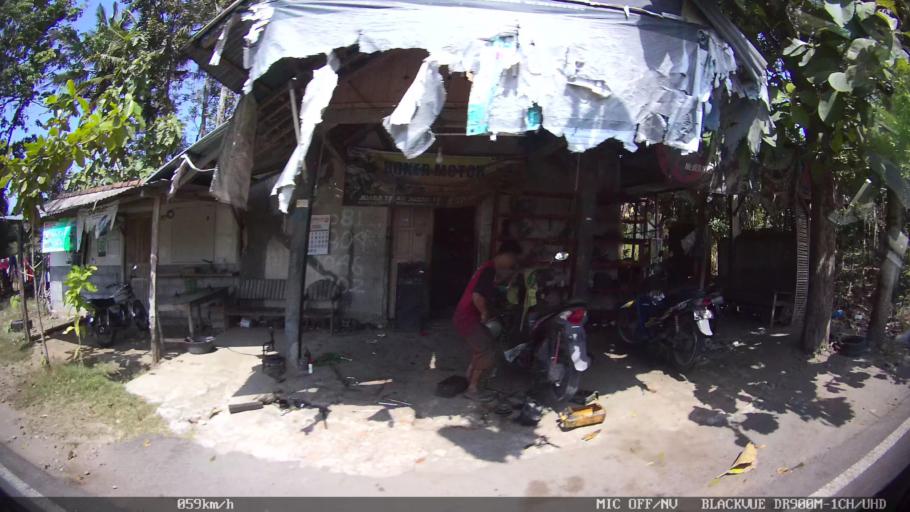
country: ID
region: Daerah Istimewa Yogyakarta
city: Pundong
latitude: -7.9718
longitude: 110.3498
